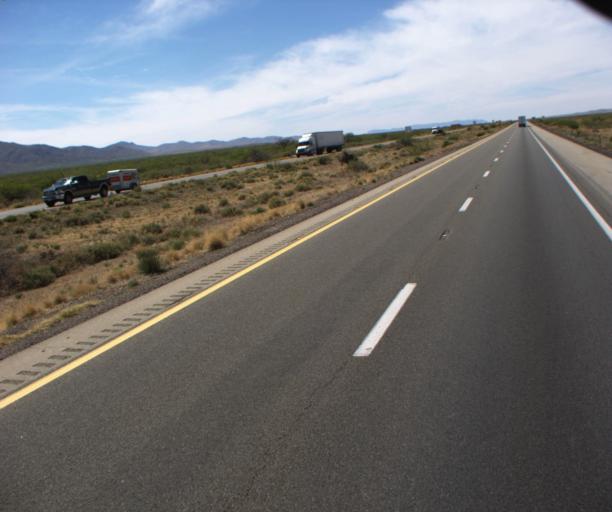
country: US
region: Arizona
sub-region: Cochise County
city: Willcox
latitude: 32.3343
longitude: -109.5284
